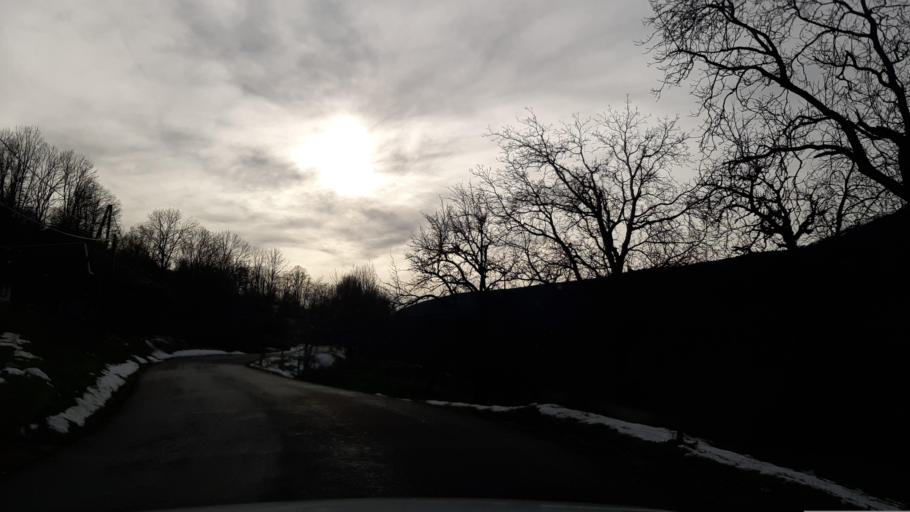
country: FR
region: Rhone-Alpes
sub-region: Departement de la Haute-Savoie
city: Cusy
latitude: 45.6637
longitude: 6.0973
